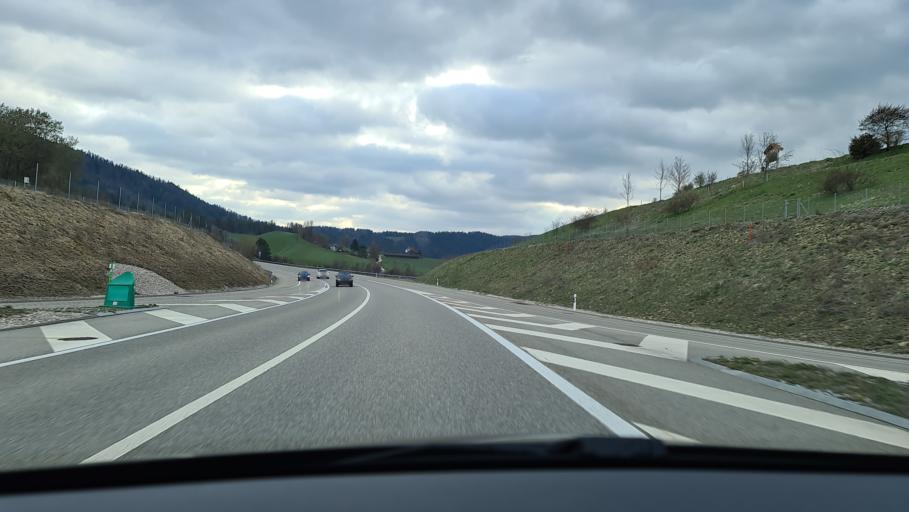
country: CH
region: Bern
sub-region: Jura bernois
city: Reconvilier
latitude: 47.2276
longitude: 7.2206
